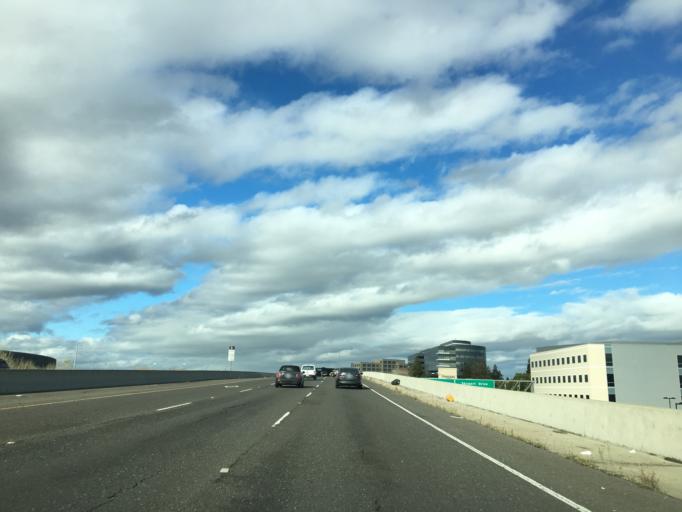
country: US
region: California
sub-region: Santa Clara County
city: San Jose
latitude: 37.3626
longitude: -121.9174
